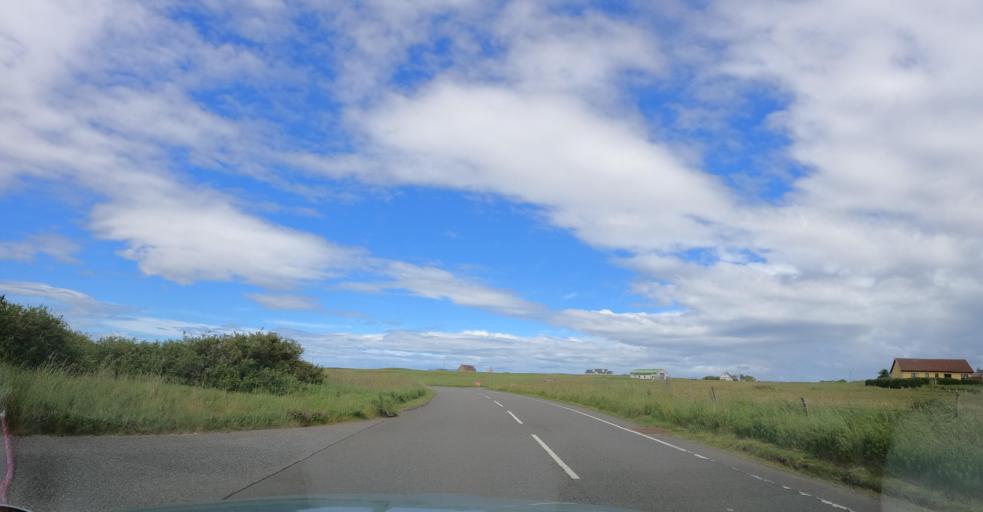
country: GB
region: Scotland
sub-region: Eilean Siar
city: Stornoway
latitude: 58.2111
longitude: -6.3223
